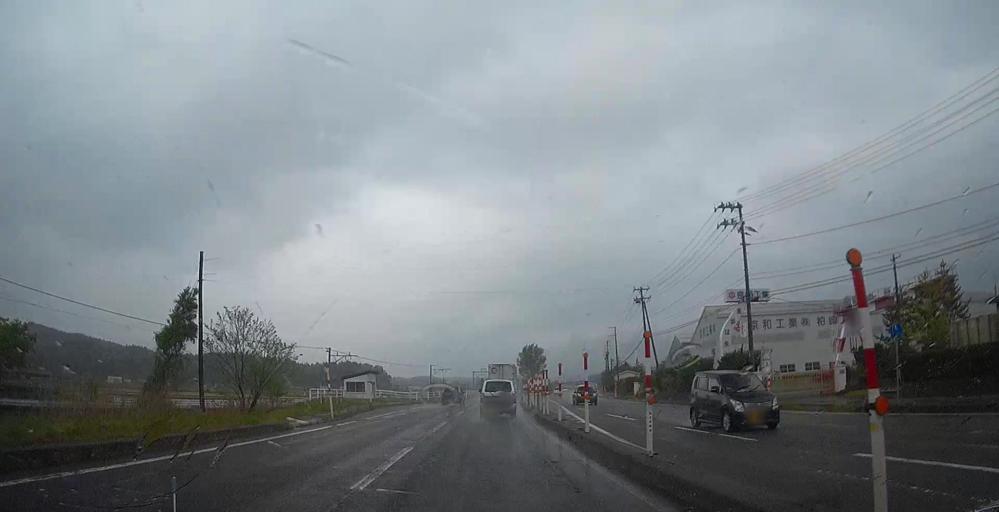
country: JP
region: Niigata
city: Kashiwazaki
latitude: 37.4442
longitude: 138.6341
